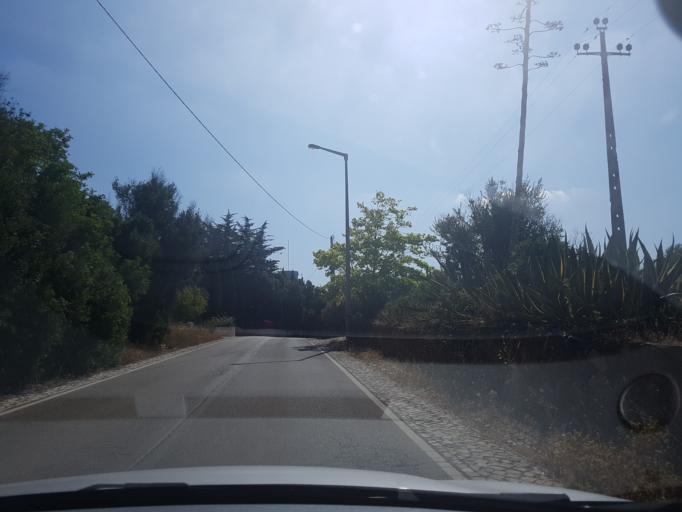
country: PT
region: Faro
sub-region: Lagoa
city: Carvoeiro
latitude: 37.0917
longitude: -8.4430
